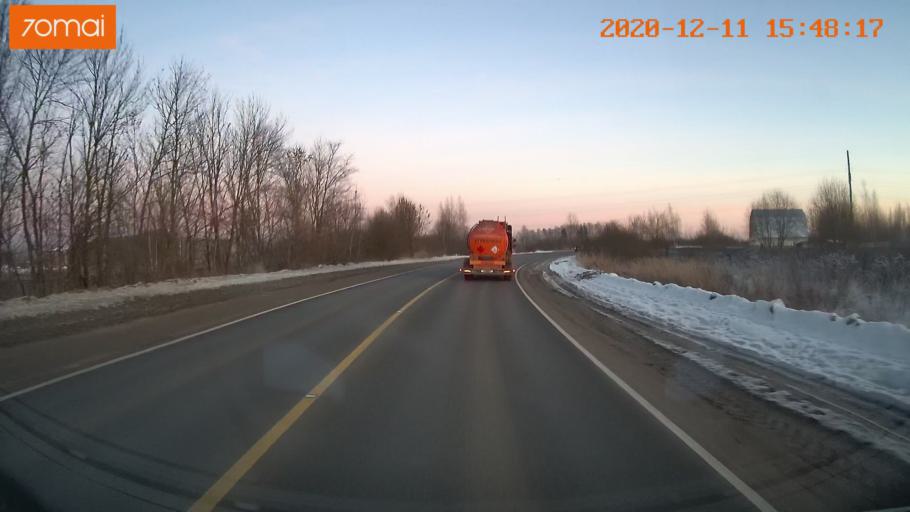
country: RU
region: Ivanovo
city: Novo-Talitsy
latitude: 56.9931
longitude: 40.8659
